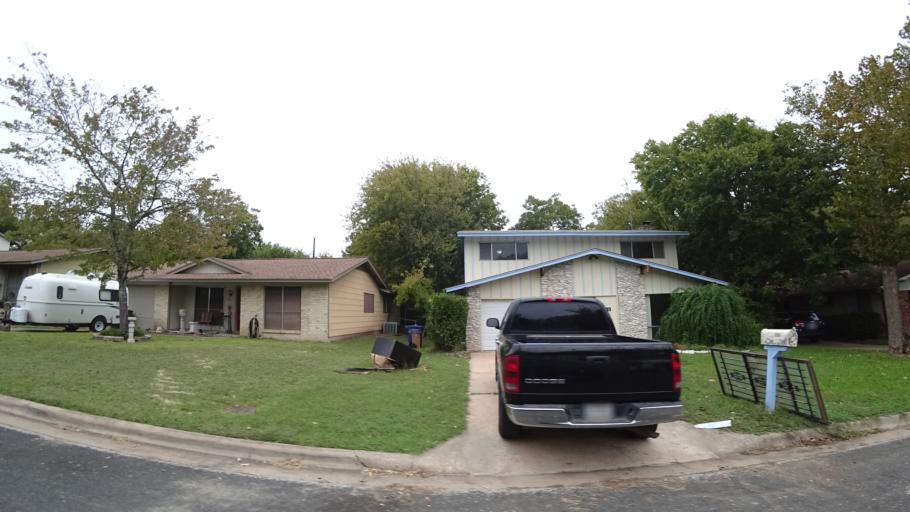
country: US
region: Texas
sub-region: Travis County
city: Austin
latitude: 30.2098
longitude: -97.7784
